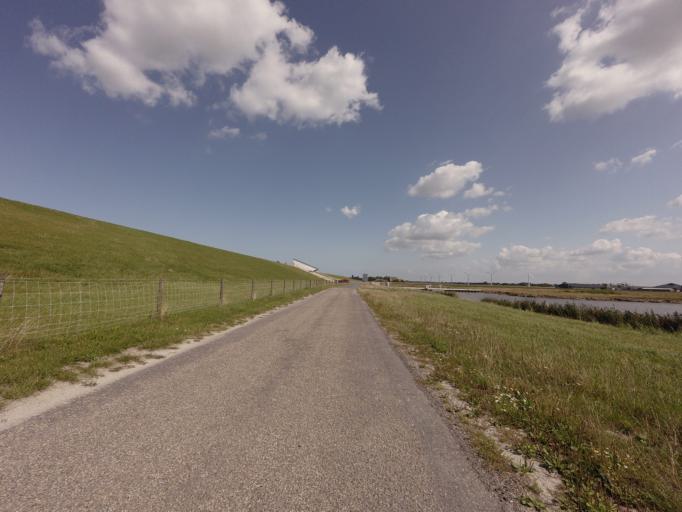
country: NL
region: Friesland
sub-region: Gemeente Ferwerderadiel
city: Hallum
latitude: 53.3205
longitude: 5.7579
